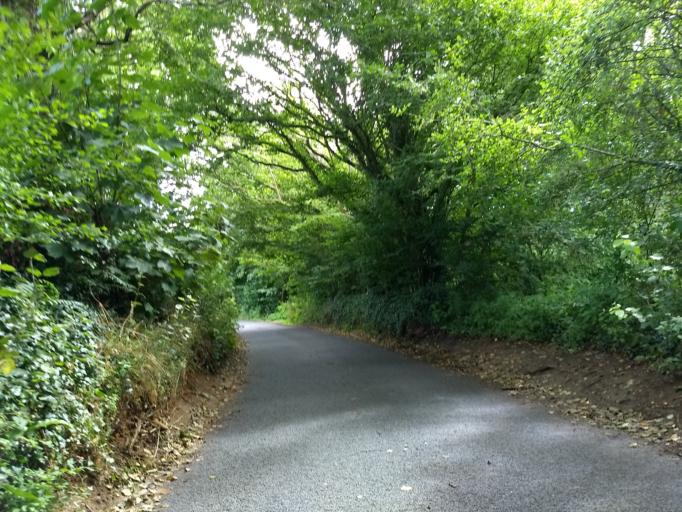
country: GB
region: England
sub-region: Isle of Wight
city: Newport
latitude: 50.6741
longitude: -1.2937
